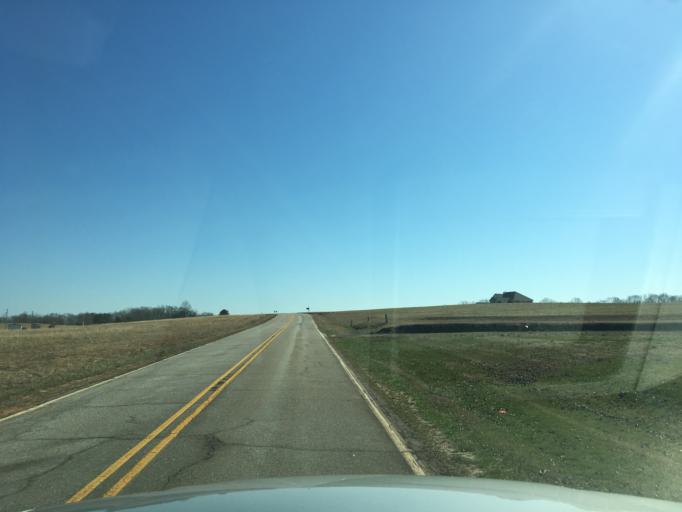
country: US
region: South Carolina
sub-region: Pickens County
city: Liberty
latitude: 34.8192
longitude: -82.7774
